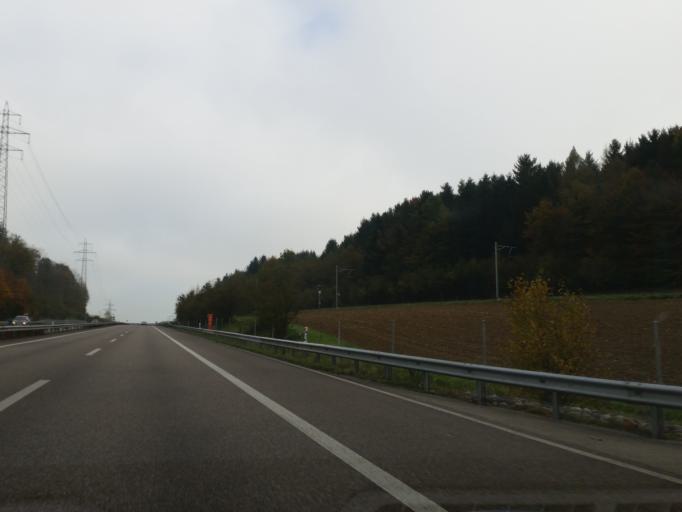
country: CH
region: Aargau
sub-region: Bezirk Zofingen
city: Safenwil
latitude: 47.3214
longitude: 7.9644
